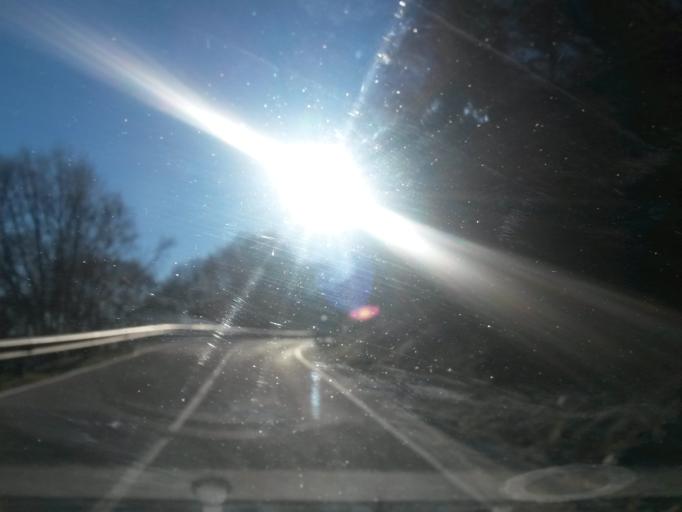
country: ES
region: Catalonia
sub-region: Provincia de Girona
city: Sant Feliu de Pallerols
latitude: 42.0538
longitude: 2.5065
